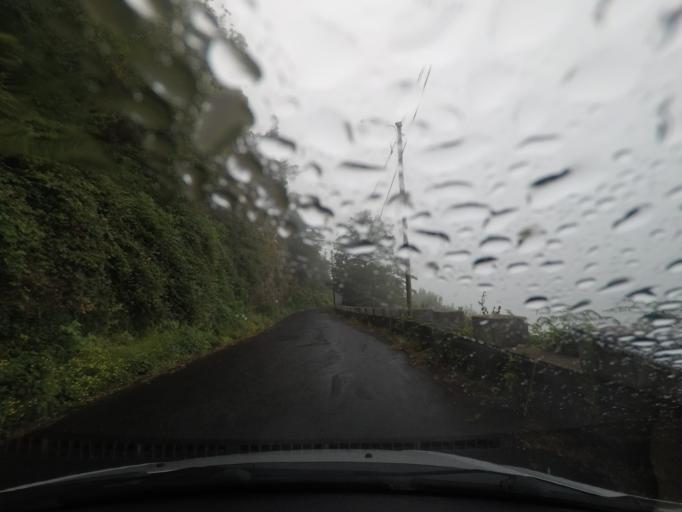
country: PT
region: Madeira
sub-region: Santana
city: Santana
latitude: 32.7564
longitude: -16.8718
